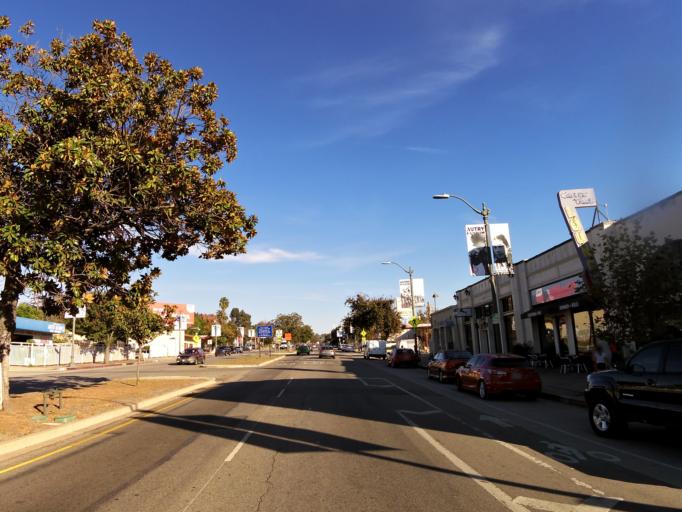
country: US
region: California
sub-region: Los Angeles County
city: Glendale
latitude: 34.1391
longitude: -118.2106
